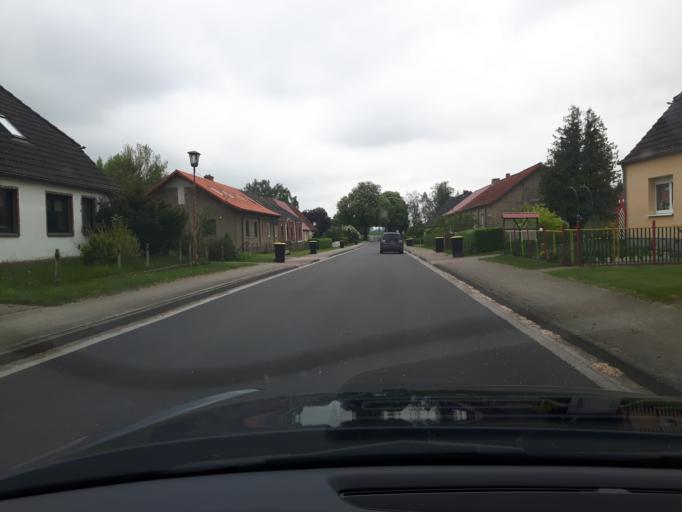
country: DE
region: Mecklenburg-Vorpommern
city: Gnoien
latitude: 54.0302
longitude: 12.6656
